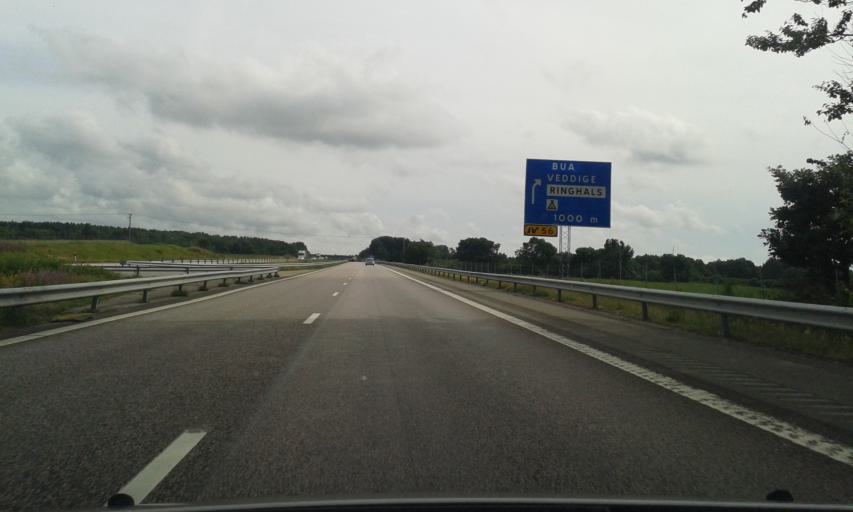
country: SE
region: Halland
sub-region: Kungsbacka Kommun
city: Frillesas
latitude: 57.2595
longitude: 12.2161
